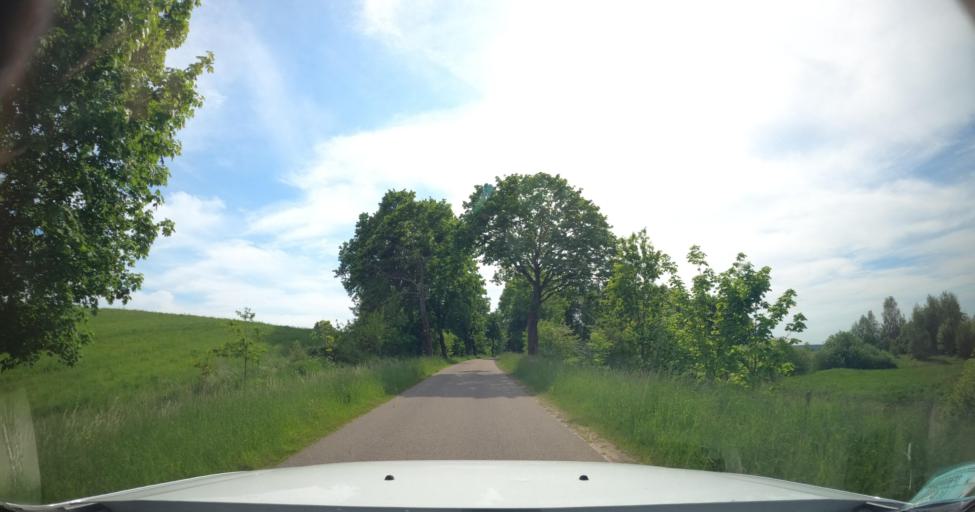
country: PL
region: Warmian-Masurian Voivodeship
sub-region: Powiat lidzbarski
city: Lubomino
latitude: 54.0913
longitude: 20.3029
